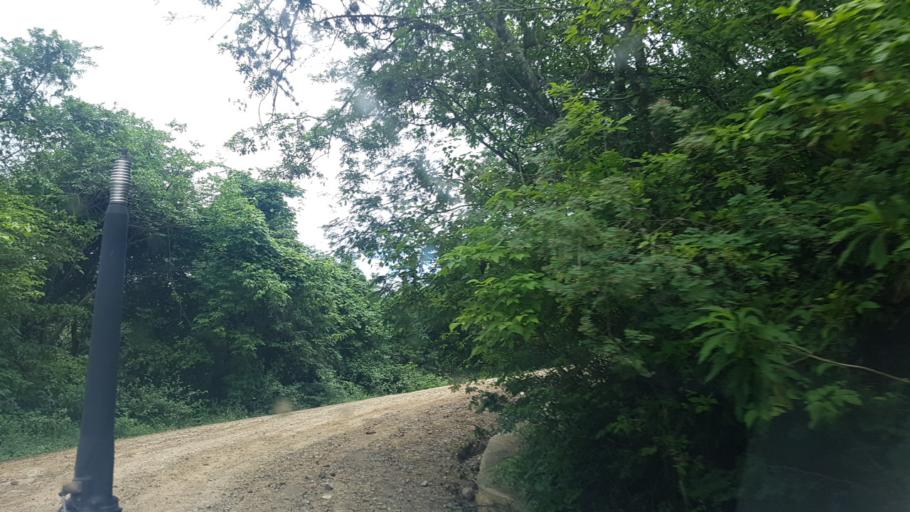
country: HN
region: El Paraiso
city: Oropoli
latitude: 13.7388
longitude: -86.7018
